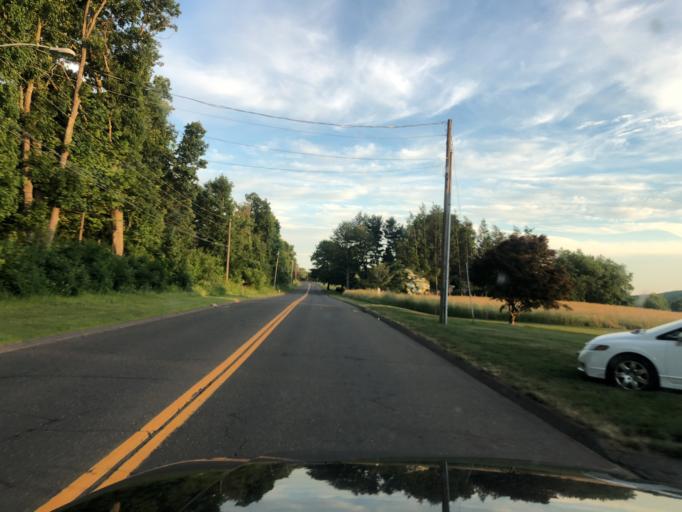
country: US
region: Connecticut
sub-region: Middlesex County
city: Middletown
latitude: 41.5594
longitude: -72.7125
